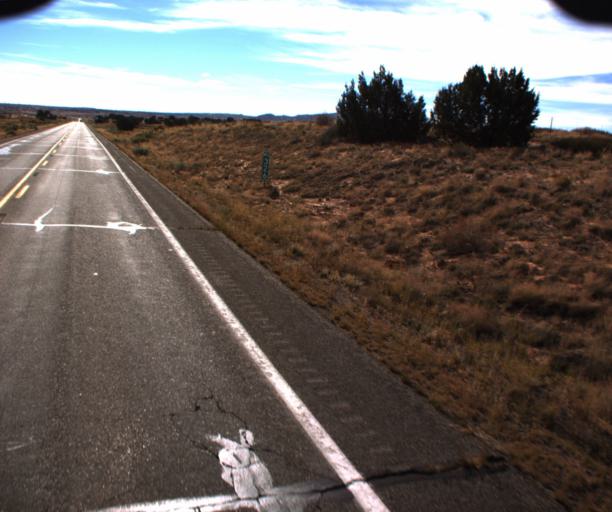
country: US
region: Arizona
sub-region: Coconino County
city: Kaibito
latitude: 36.5976
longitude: -111.1668
